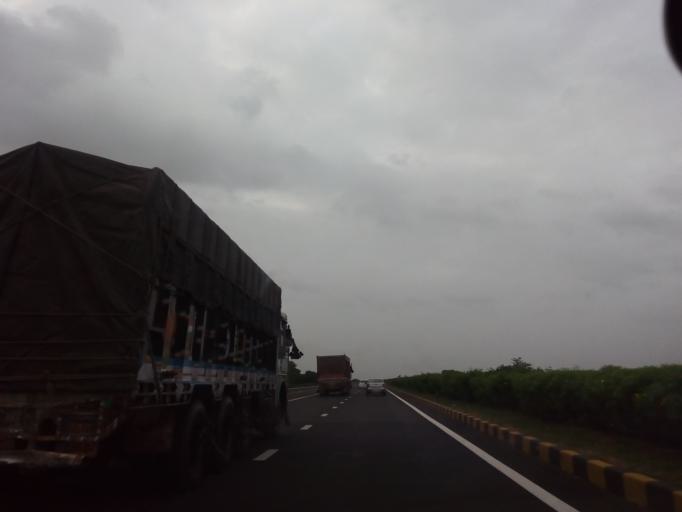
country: IN
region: Gujarat
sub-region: Kheda
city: Nadiad
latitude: 22.7184
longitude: 72.8804
